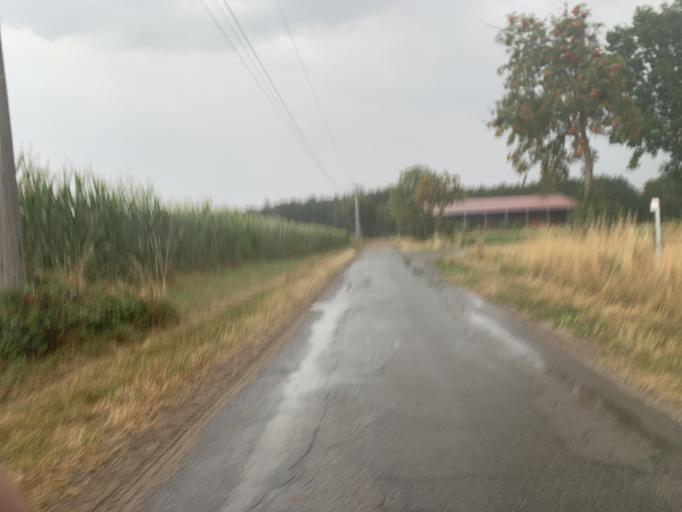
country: DE
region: Lower Saxony
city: Thomasburg
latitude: 53.2180
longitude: 10.6383
